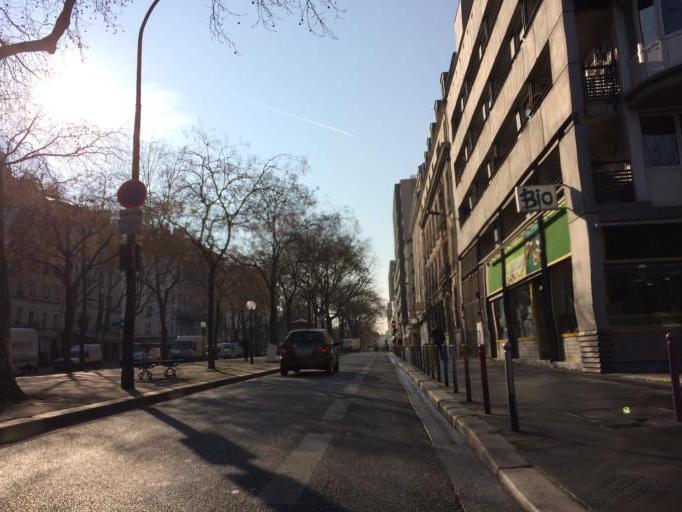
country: FR
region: Ile-de-France
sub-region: Departement de Seine-Saint-Denis
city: Bagnolet
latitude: 48.8550
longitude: 2.3954
